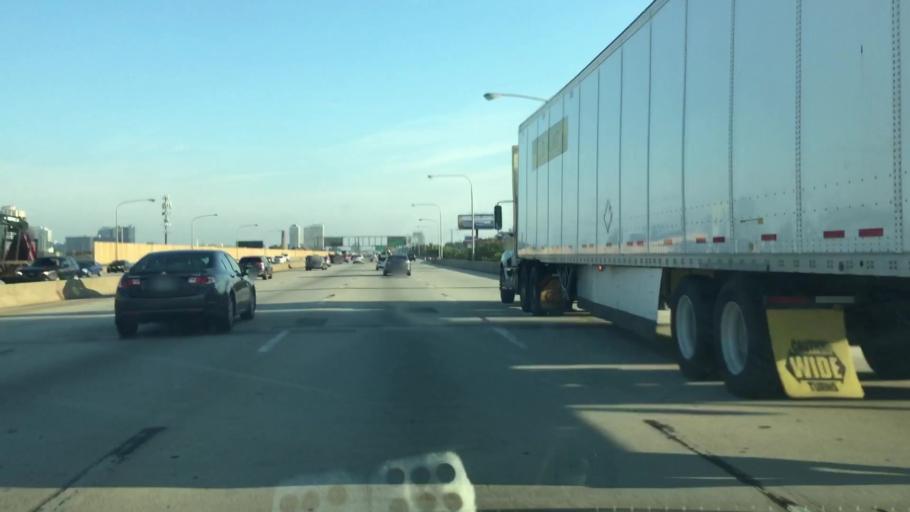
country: US
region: New Jersey
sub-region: Camden County
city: Camden
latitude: 39.9240
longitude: -75.1485
